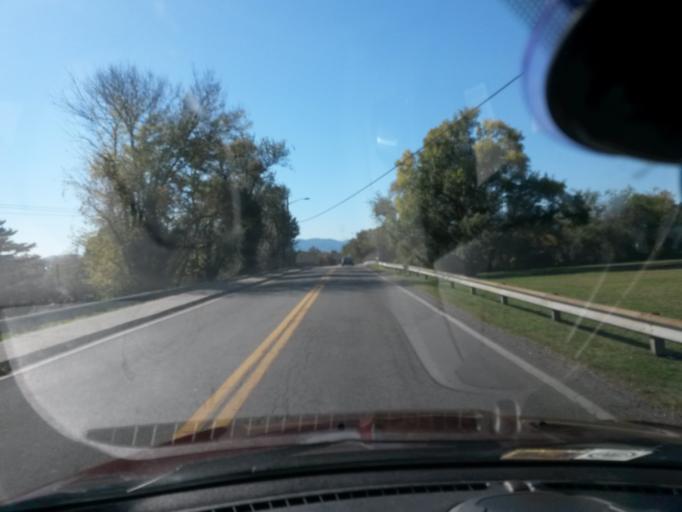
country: US
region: Virginia
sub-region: City of Roanoke
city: Roanoke
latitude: 37.2912
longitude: -79.9402
